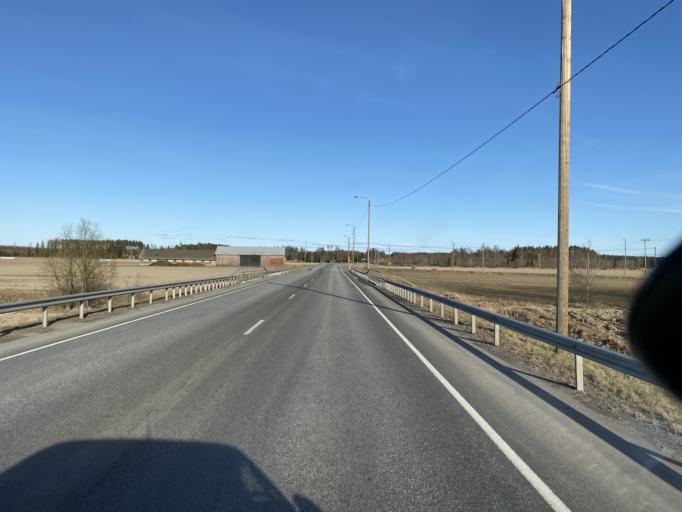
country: FI
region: Satakunta
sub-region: Pori
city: Huittinen
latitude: 61.1774
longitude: 22.5950
